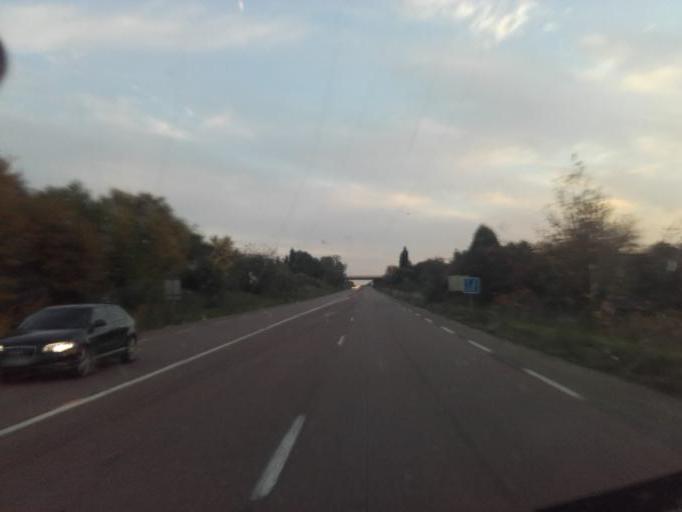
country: FR
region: Bourgogne
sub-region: Departement de Saone-et-Loire
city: Chagny
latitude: 46.9070
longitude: 4.7595
